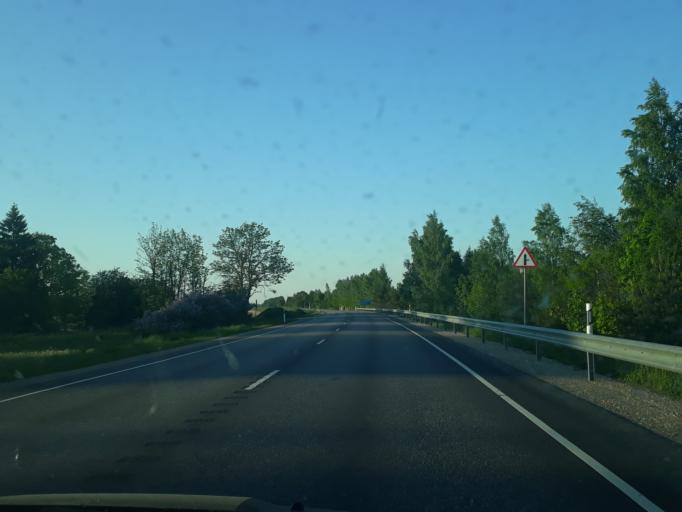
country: EE
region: Paernumaa
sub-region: Tootsi vald
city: Tootsi
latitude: 58.5840
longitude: 24.8948
